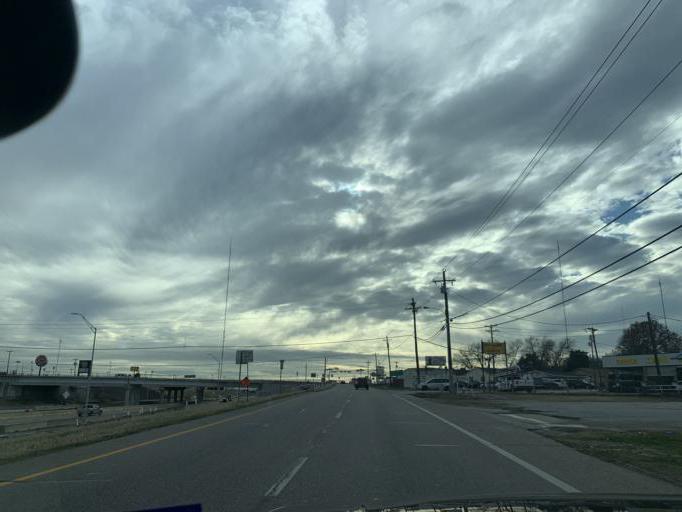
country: US
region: Texas
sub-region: Dallas County
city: Cedar Hill
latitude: 32.5915
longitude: -96.9454
